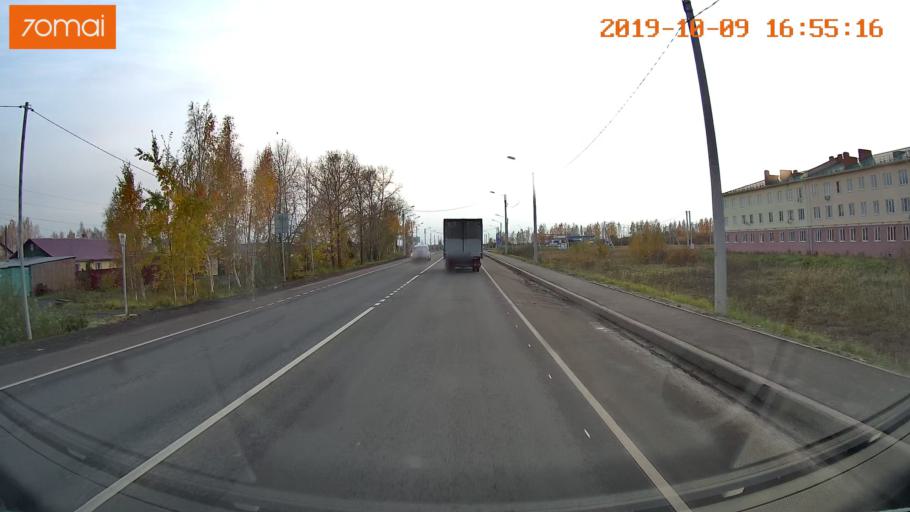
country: RU
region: Ivanovo
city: Privolzhsk
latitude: 57.3689
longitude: 41.2750
